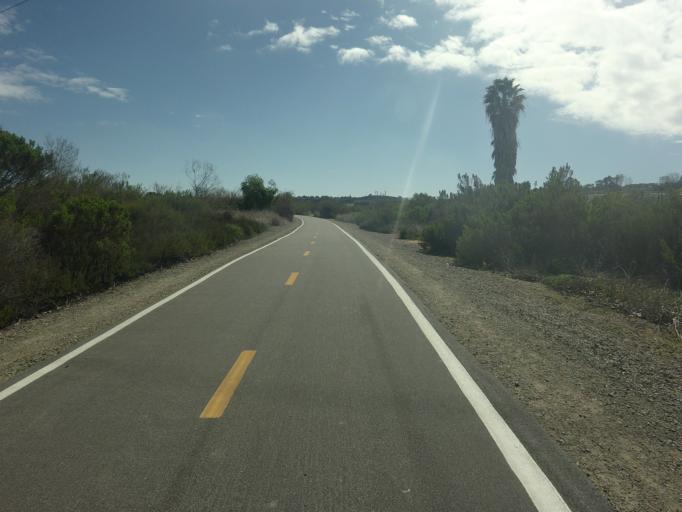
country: US
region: California
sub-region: Orange County
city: Aliso Viejo
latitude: 33.5636
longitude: -117.7185
